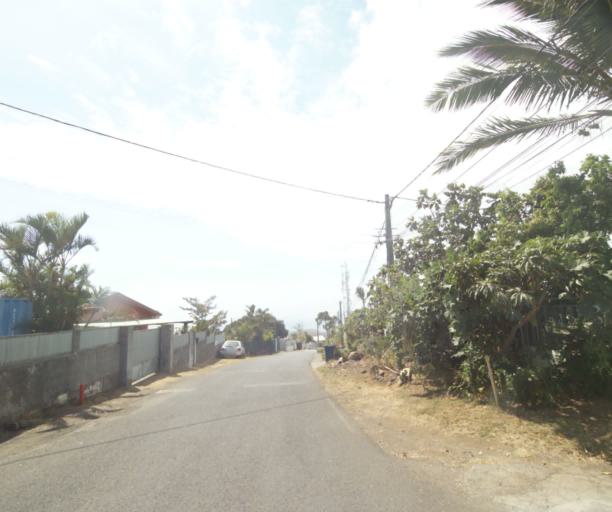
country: RE
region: Reunion
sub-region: Reunion
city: Saint-Paul
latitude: -21.0569
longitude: 55.2564
